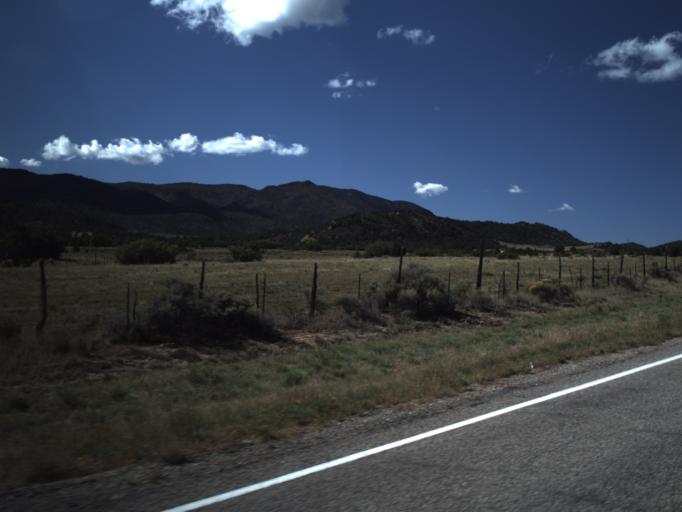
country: US
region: Utah
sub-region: Iron County
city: Cedar City
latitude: 37.6308
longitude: -113.3058
